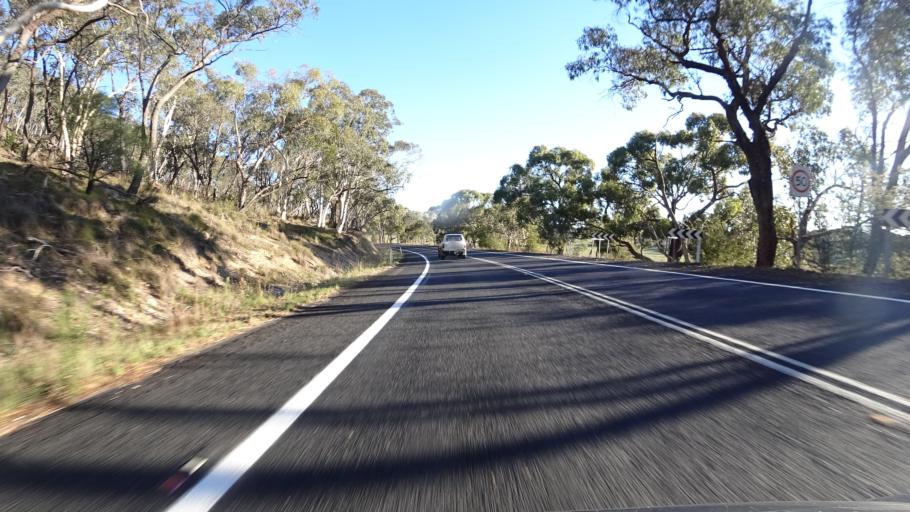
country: AU
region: New South Wales
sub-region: Lithgow
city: Portland
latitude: -33.3059
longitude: 150.0320
